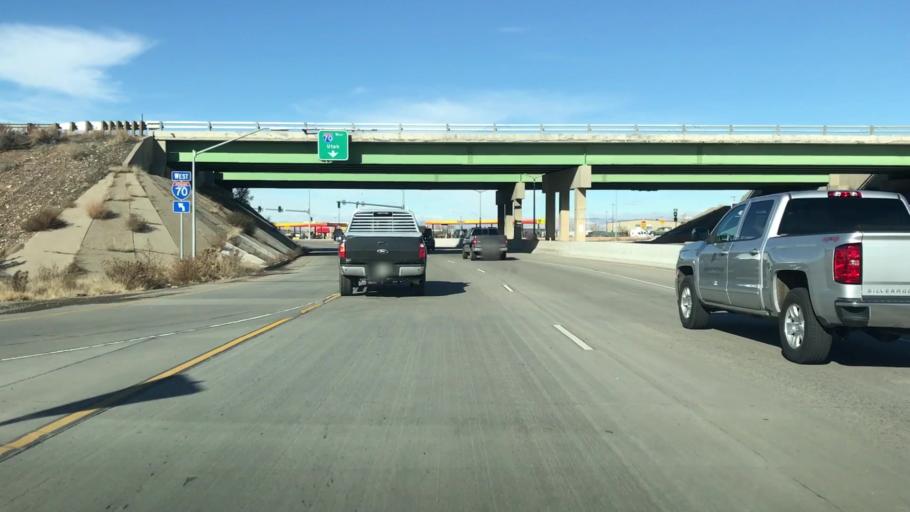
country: US
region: Colorado
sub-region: Mesa County
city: Redlands
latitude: 39.1116
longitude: -108.6439
